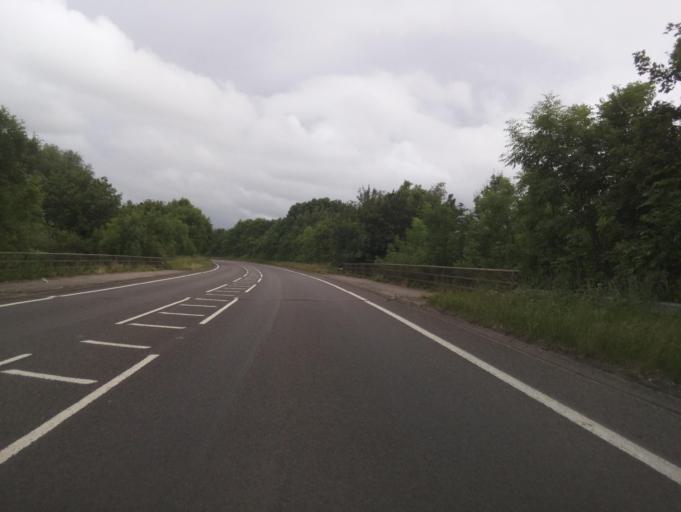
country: GB
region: England
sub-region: Staffordshire
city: Burton upon Trent
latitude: 52.8589
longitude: -1.6797
